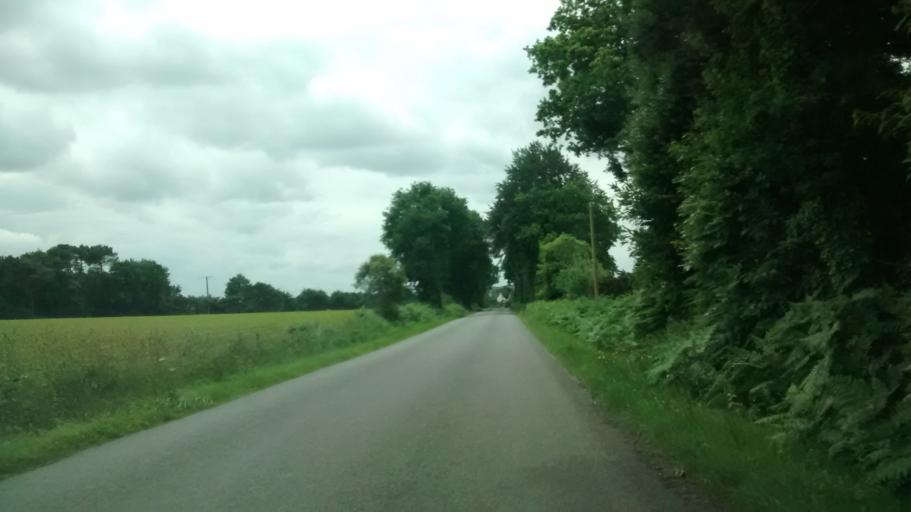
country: FR
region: Brittany
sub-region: Departement du Morbihan
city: Ruffiac
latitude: 47.8229
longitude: -2.2707
